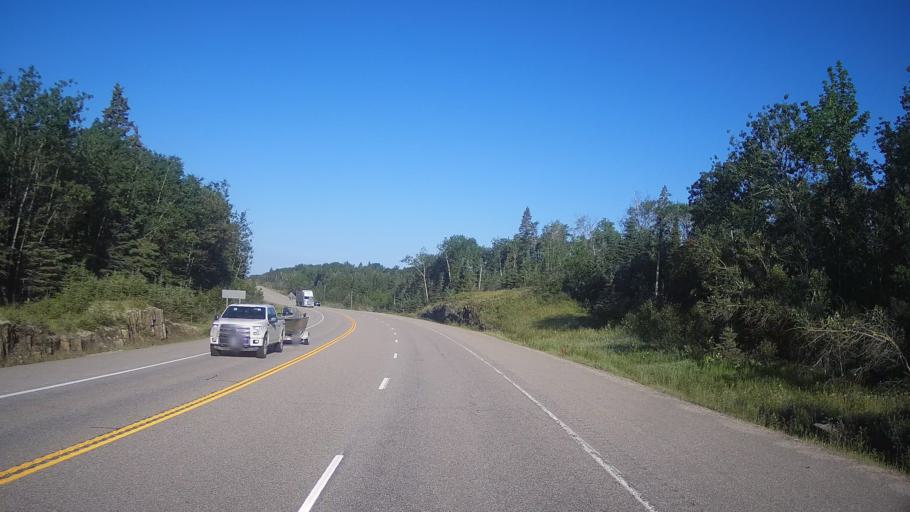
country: US
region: Minnesota
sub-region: Roseau County
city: Warroad
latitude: 49.7189
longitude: -94.7286
